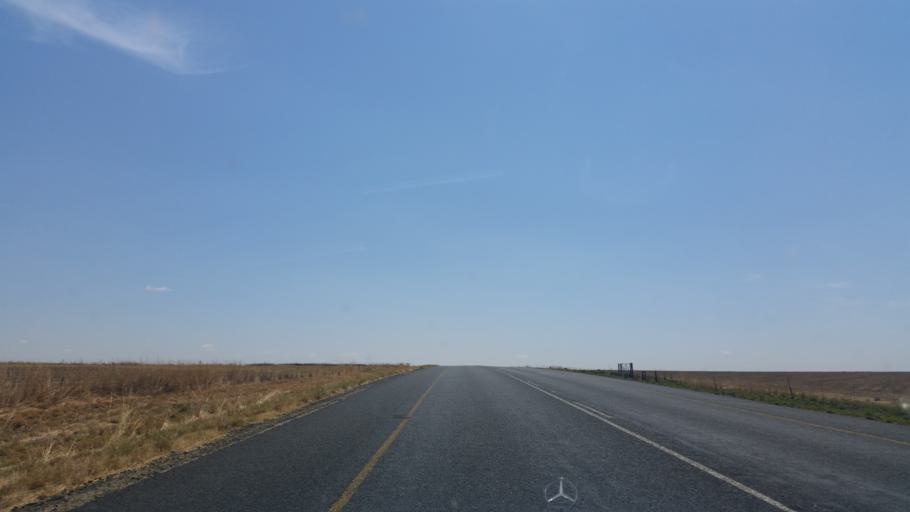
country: ZA
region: Orange Free State
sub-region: Thabo Mofutsanyana District Municipality
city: Phuthaditjhaba
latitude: -28.1884
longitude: 28.6862
